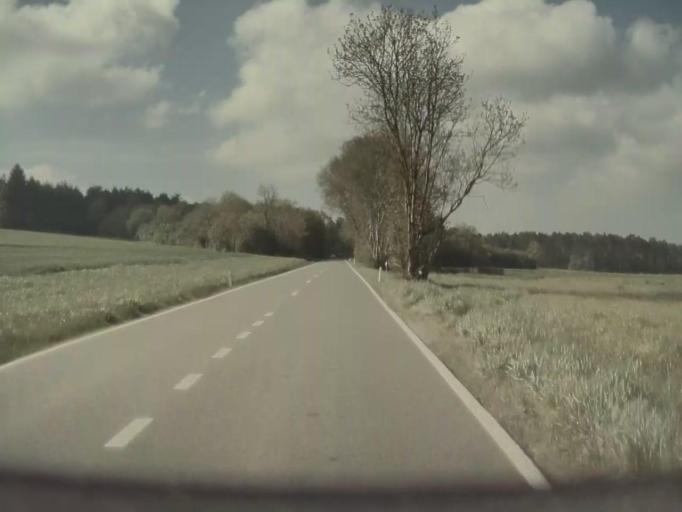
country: BE
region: Wallonia
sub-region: Province du Luxembourg
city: Tellin
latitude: 50.1045
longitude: 5.2331
